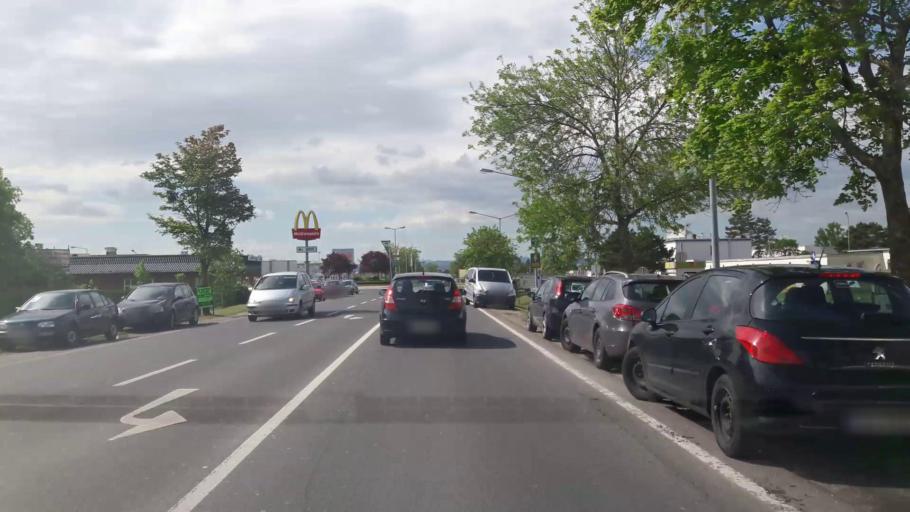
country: AT
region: Lower Austria
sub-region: Politischer Bezirk Wiener Neustadt
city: Theresienfeld
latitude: 47.8448
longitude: 16.2459
